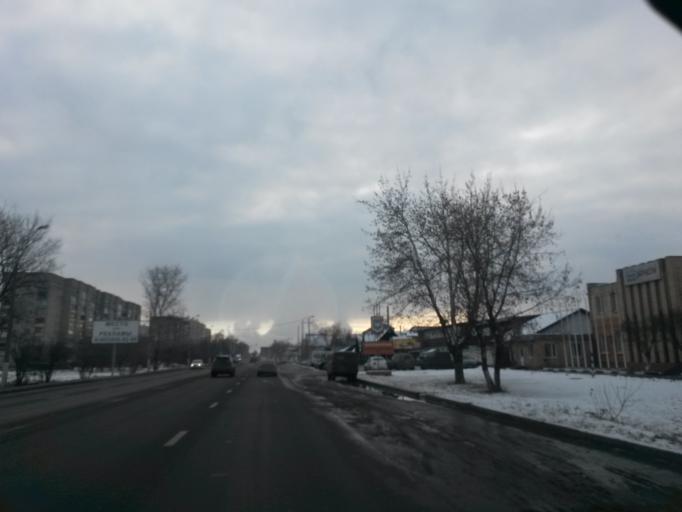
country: RU
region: Moskovskaya
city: Klimovsk
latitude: 55.3656
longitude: 37.5311
